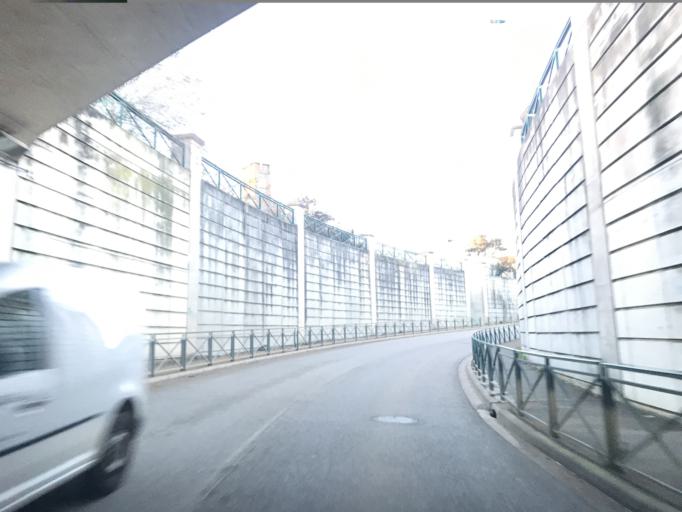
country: FR
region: Ile-de-France
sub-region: Departement des Yvelines
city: Mere
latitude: 48.8026
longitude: 1.8160
